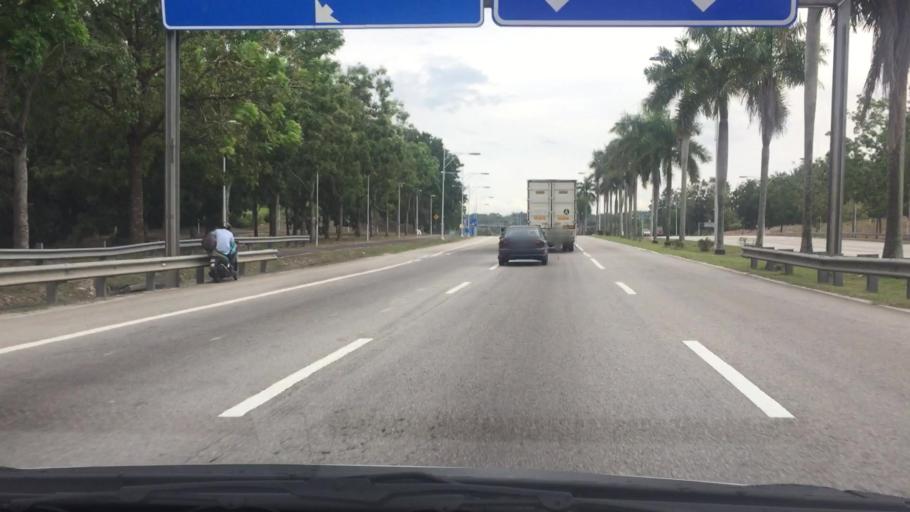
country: MY
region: Putrajaya
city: Putrajaya
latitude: 2.9003
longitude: 101.6581
